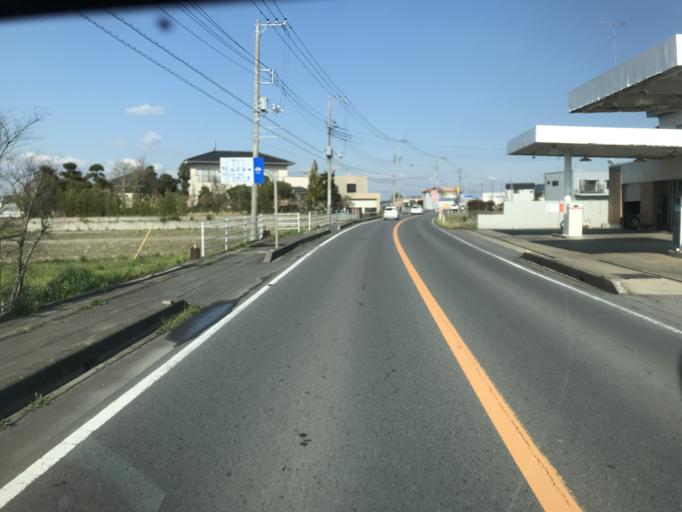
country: JP
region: Ibaraki
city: Itako
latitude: 35.9867
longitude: 140.4815
